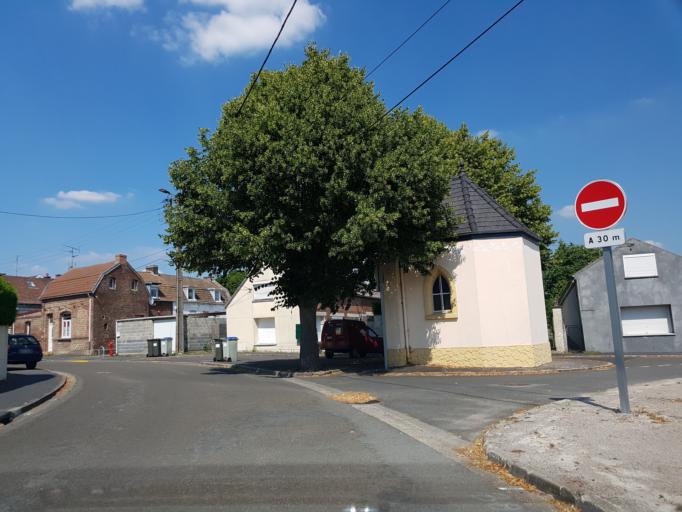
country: FR
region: Nord-Pas-de-Calais
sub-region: Departement du Nord
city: Roeulx
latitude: 50.3035
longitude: 3.3325
